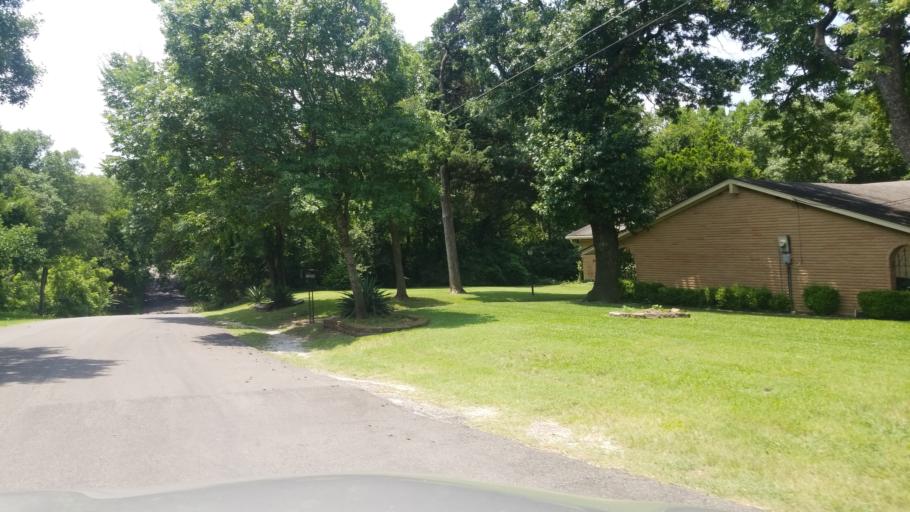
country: US
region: Texas
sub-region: Dallas County
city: Duncanville
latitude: 32.6745
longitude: -96.9158
